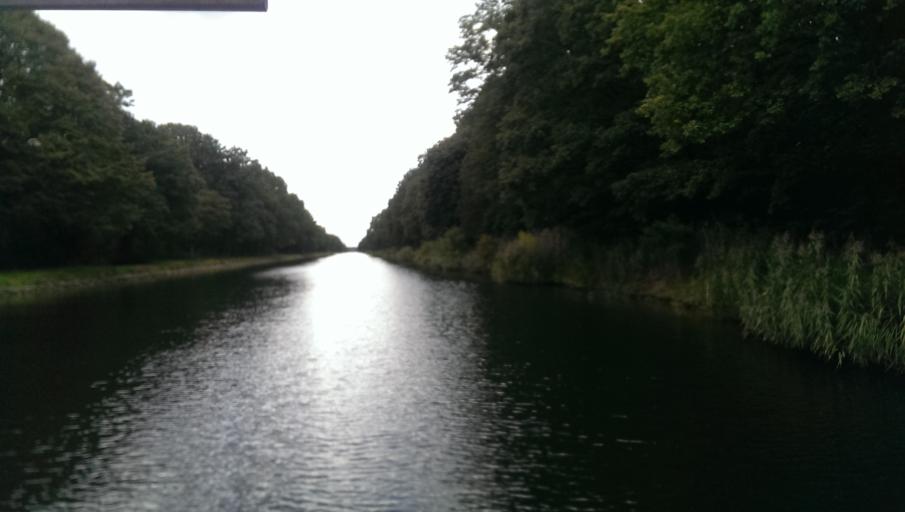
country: DE
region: Brandenburg
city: Marienwerder
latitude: 52.8498
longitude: 13.5887
